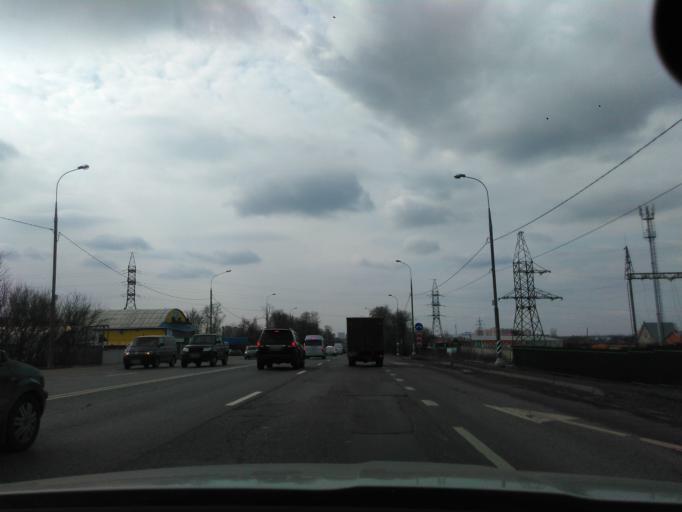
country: RU
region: Moskovskaya
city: Sheremet'yevskiy
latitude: 55.9912
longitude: 37.5321
